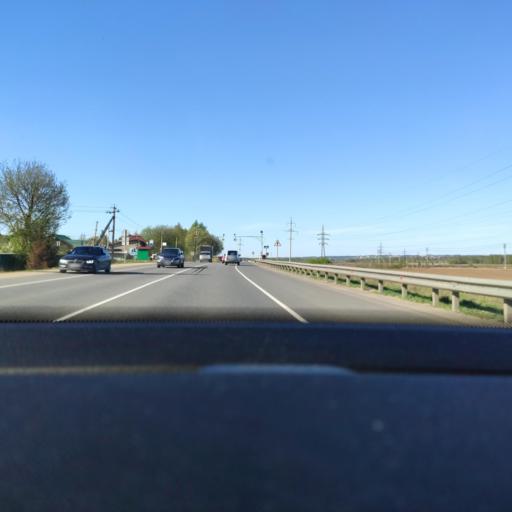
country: RU
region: Moskovskaya
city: Yakhroma
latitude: 56.3234
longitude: 37.4816
